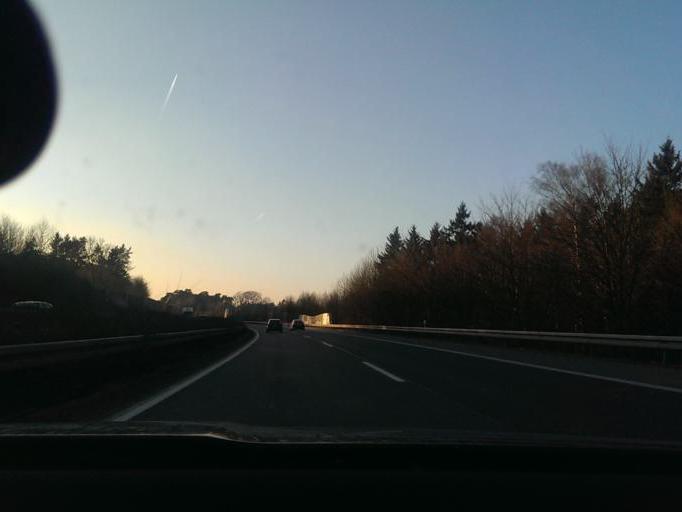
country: DE
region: North Rhine-Westphalia
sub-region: Regierungsbezirk Detmold
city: Oerlinghausen
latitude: 51.9235
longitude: 8.6112
